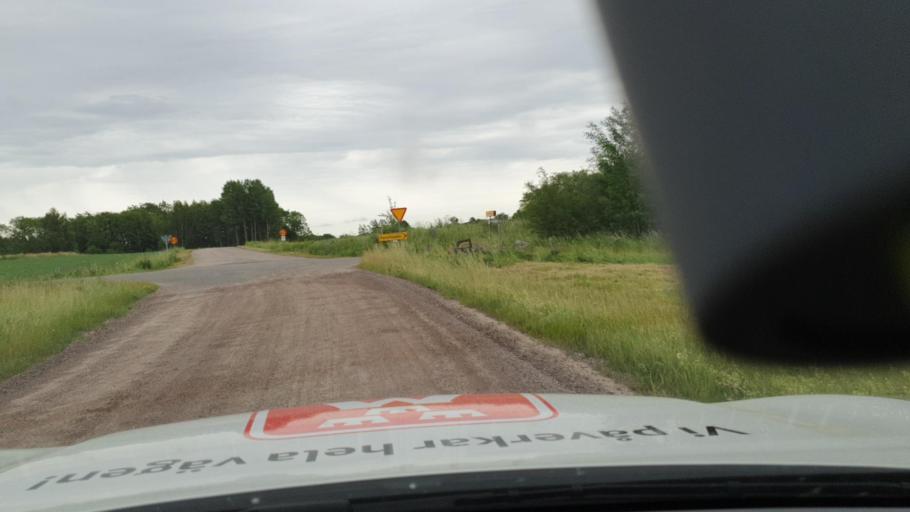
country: SE
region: Vaestra Goetaland
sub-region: Skovde Kommun
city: Skoevde
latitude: 58.3698
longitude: 13.8721
